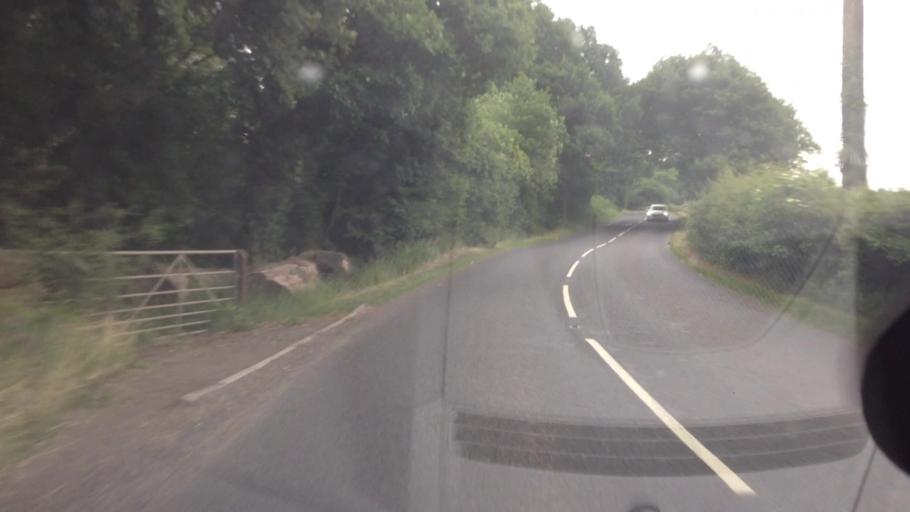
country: GB
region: England
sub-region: City and Borough of Wakefield
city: Crigglestone
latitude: 53.6192
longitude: -1.5439
